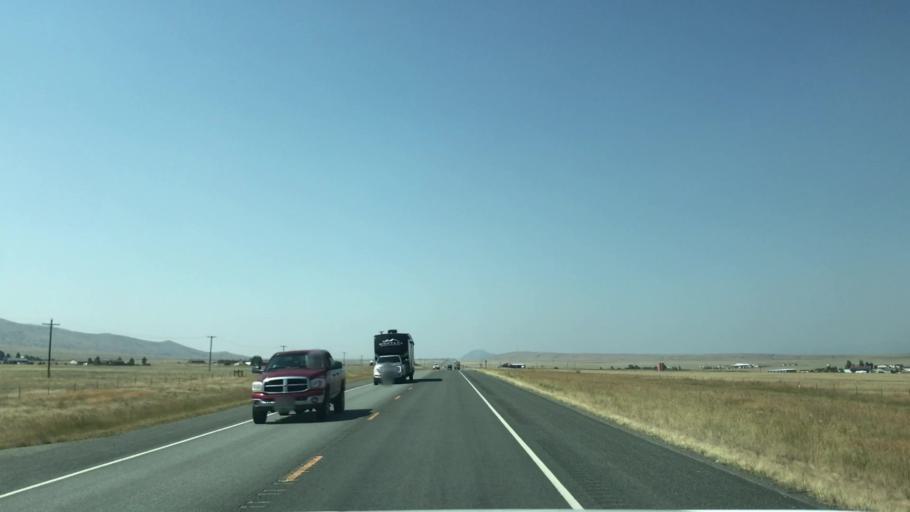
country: US
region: Montana
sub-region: Broadwater County
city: Townsend
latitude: 46.4049
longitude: -111.5902
